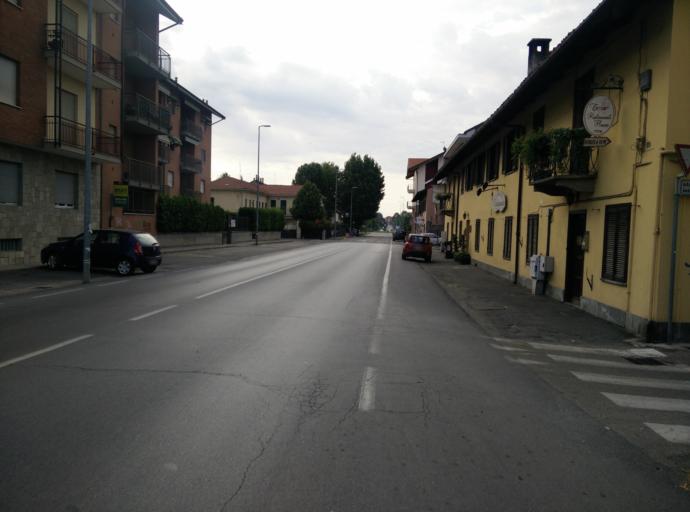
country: IT
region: Piedmont
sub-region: Provincia di Torino
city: Revigliasco
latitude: 44.9907
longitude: 7.7190
